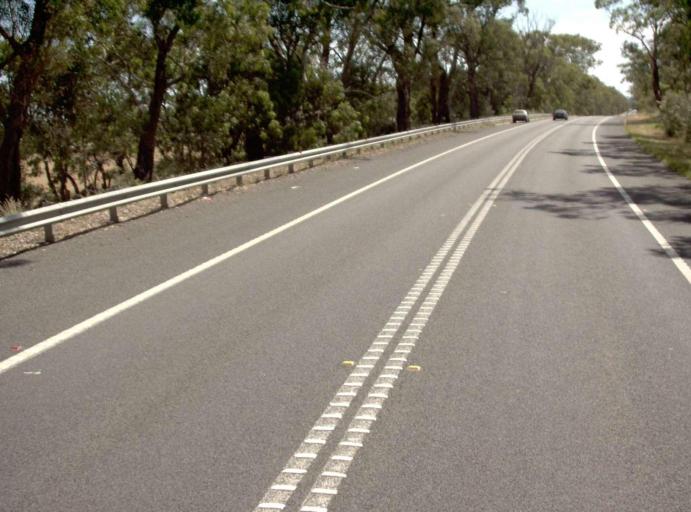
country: AU
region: Victoria
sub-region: Wellington
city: Sale
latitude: -37.9419
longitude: 147.1428
